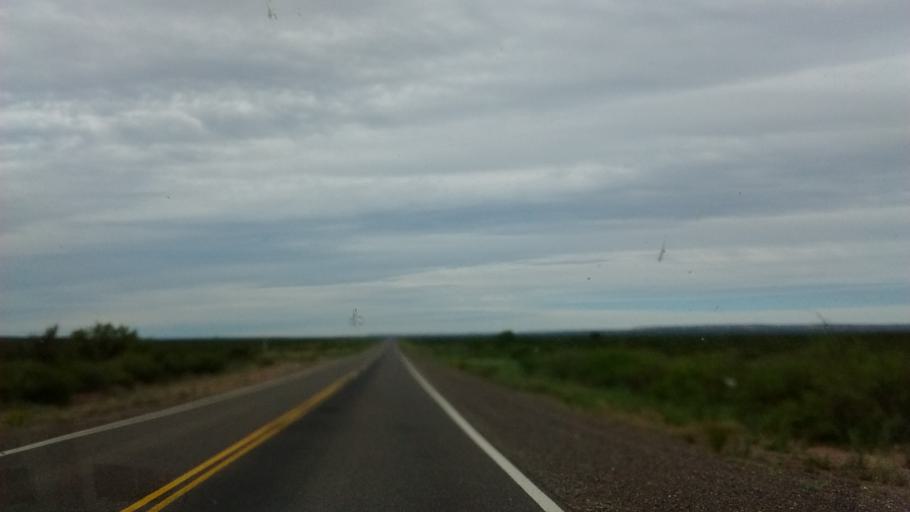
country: AR
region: Rio Negro
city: Catriel
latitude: -38.0656
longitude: -67.9222
